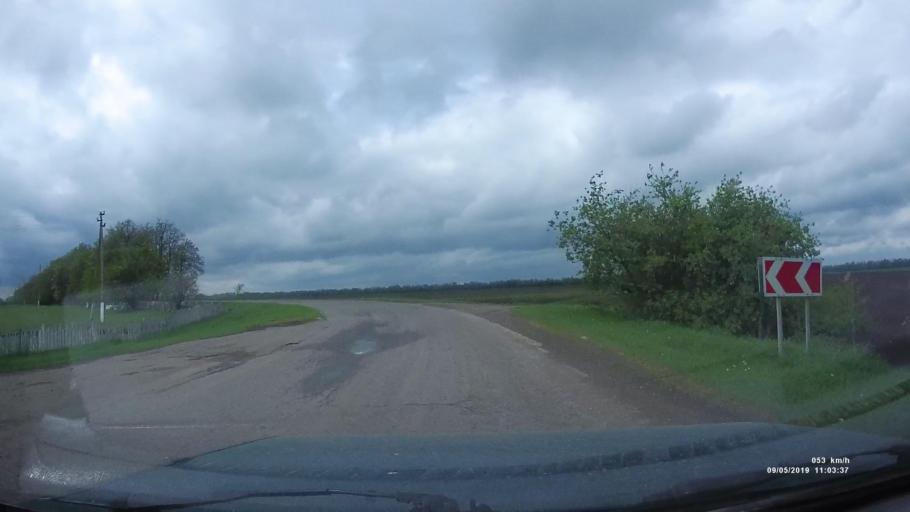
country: RU
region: Krasnodarskiy
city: Kanelovskaya
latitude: 46.8259
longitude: 39.2102
